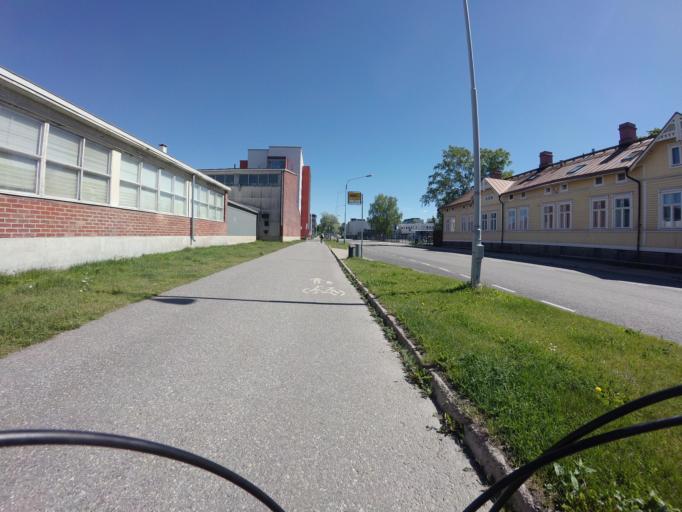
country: FI
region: Varsinais-Suomi
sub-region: Turku
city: Turku
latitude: 60.4483
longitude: 22.2382
